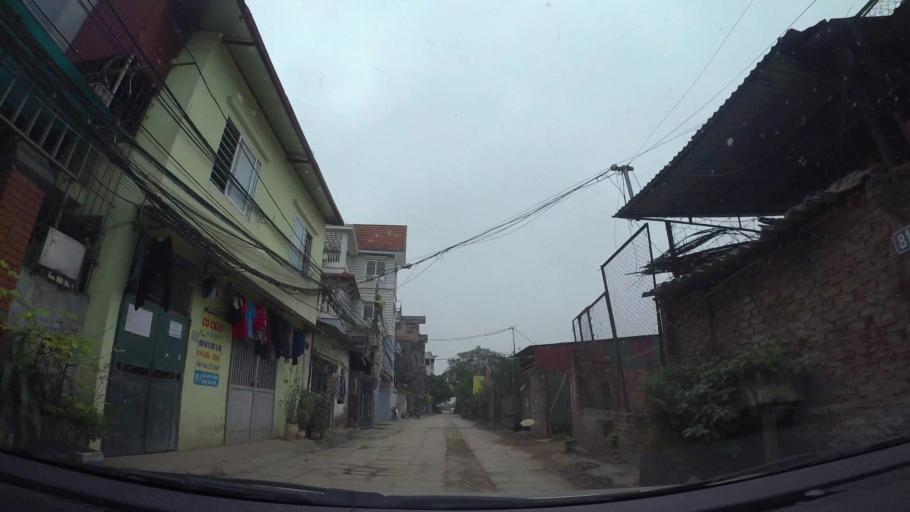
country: VN
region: Ha Noi
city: Tay Ho
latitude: 21.0672
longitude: 105.8360
